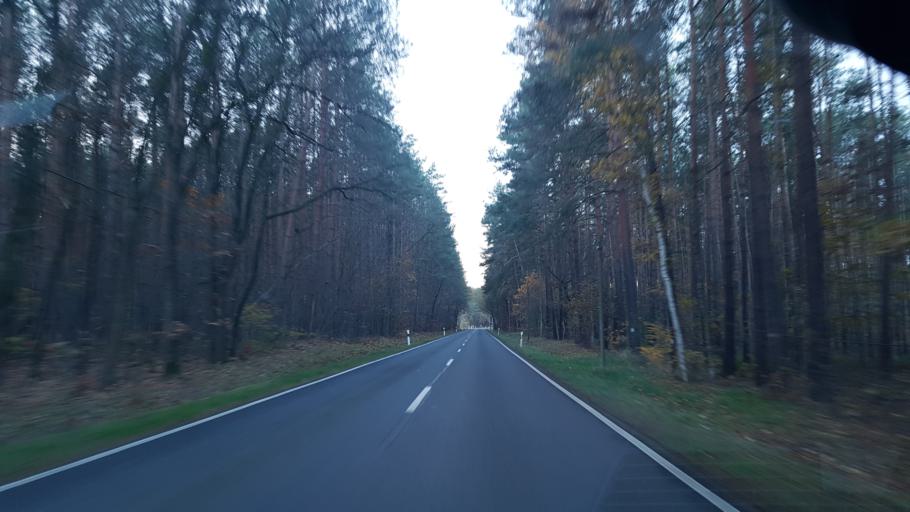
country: DE
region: Brandenburg
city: Sonnewalde
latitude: 51.7220
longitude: 13.6883
